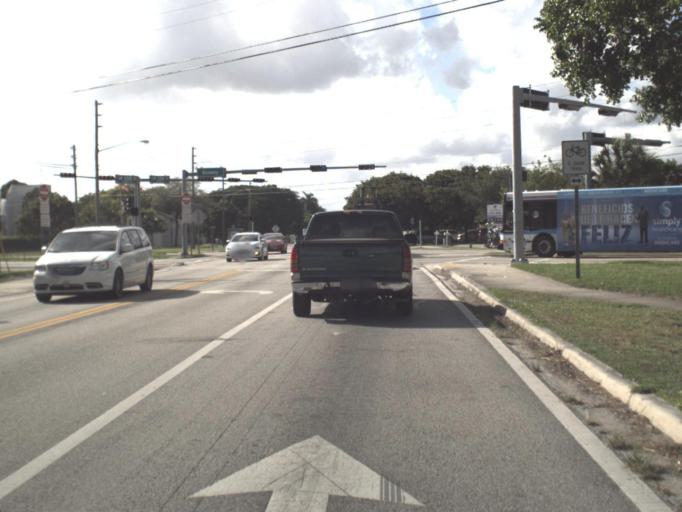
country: US
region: Florida
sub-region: Miami-Dade County
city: Leisure City
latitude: 25.4994
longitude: -80.4471
